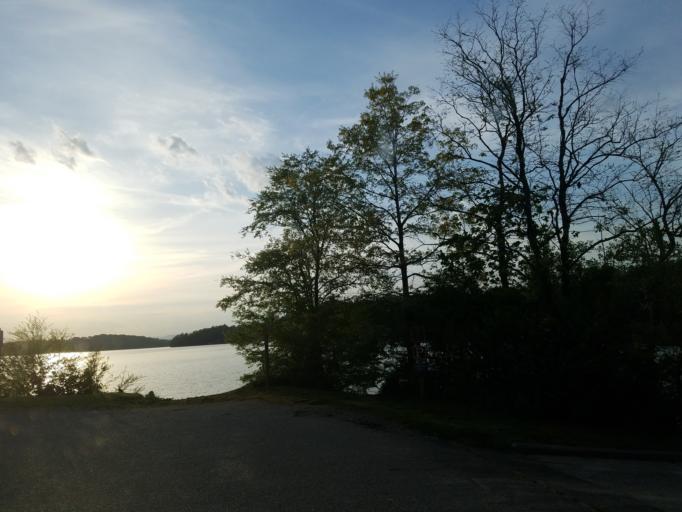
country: US
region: Georgia
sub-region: Fannin County
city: Blue Ridge
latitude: 34.8690
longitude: -84.2544
